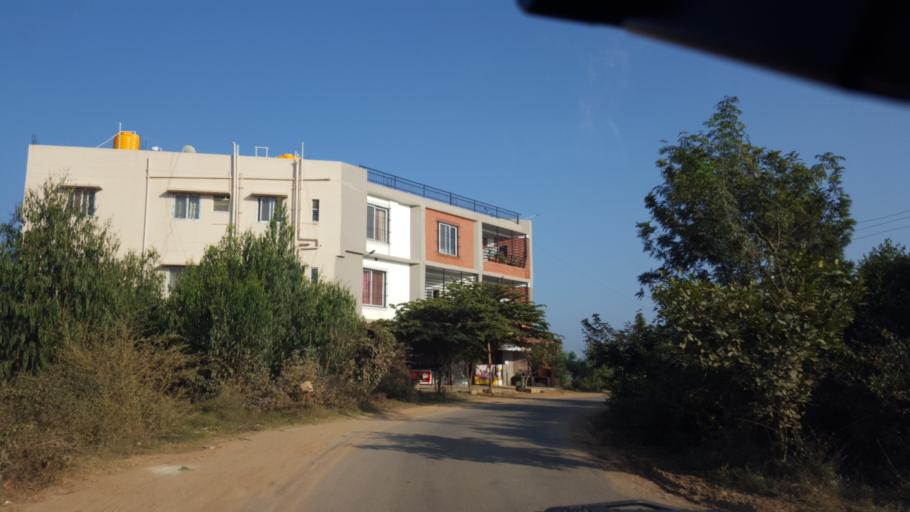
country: IN
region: Karnataka
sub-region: Bangalore Rural
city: Hoskote
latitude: 12.9234
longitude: 77.7562
